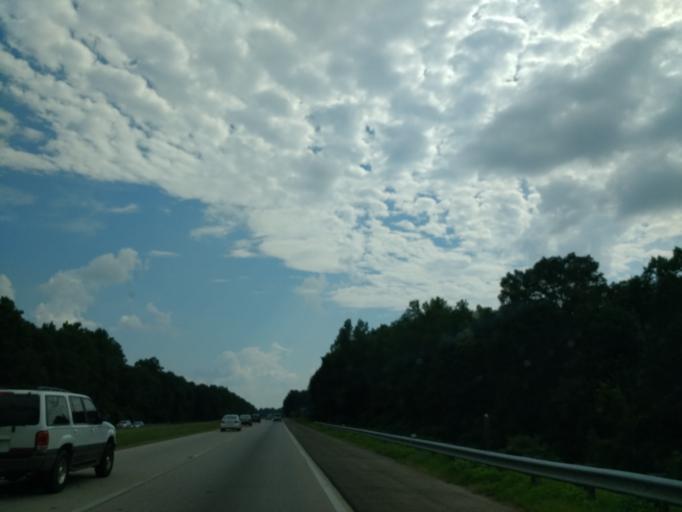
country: US
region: Georgia
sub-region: Hall County
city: Gainesville
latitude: 34.3062
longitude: -83.7911
